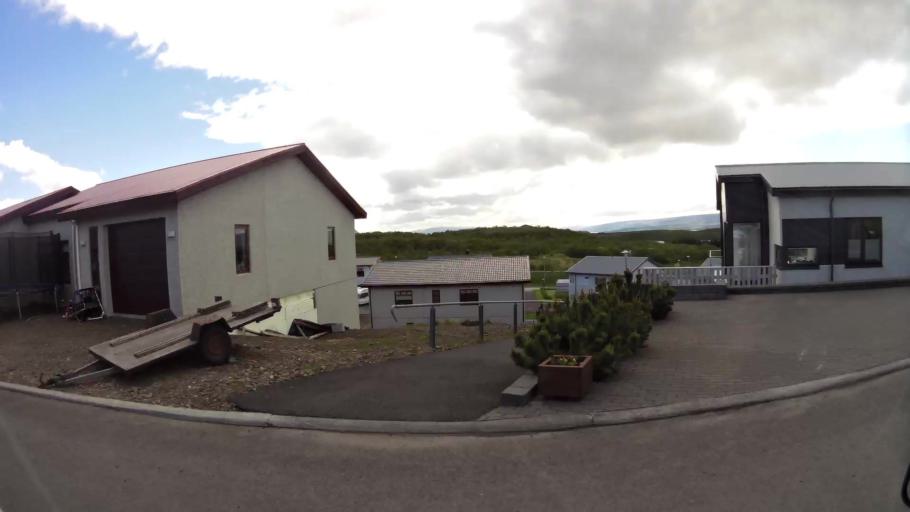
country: IS
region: East
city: Egilsstadir
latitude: 65.2587
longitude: -14.3821
